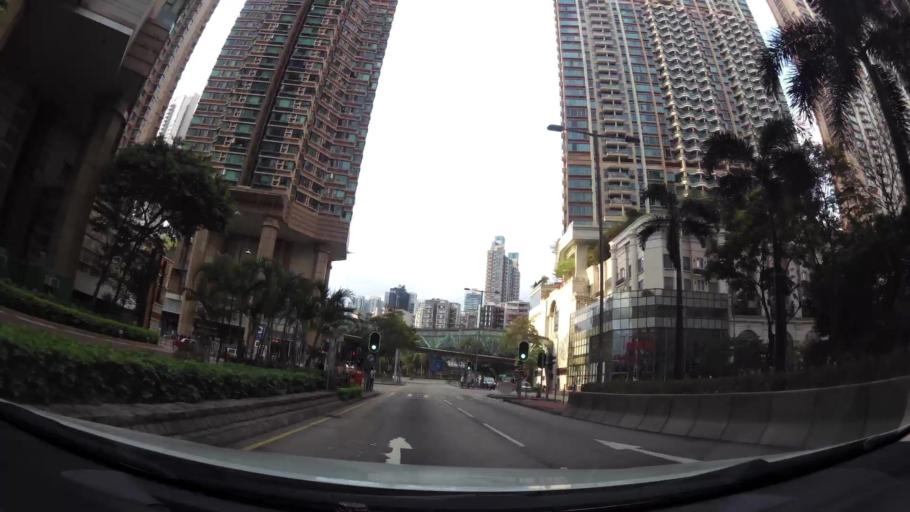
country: HK
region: Sham Shui Po
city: Sham Shui Po
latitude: 22.3167
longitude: 114.1636
